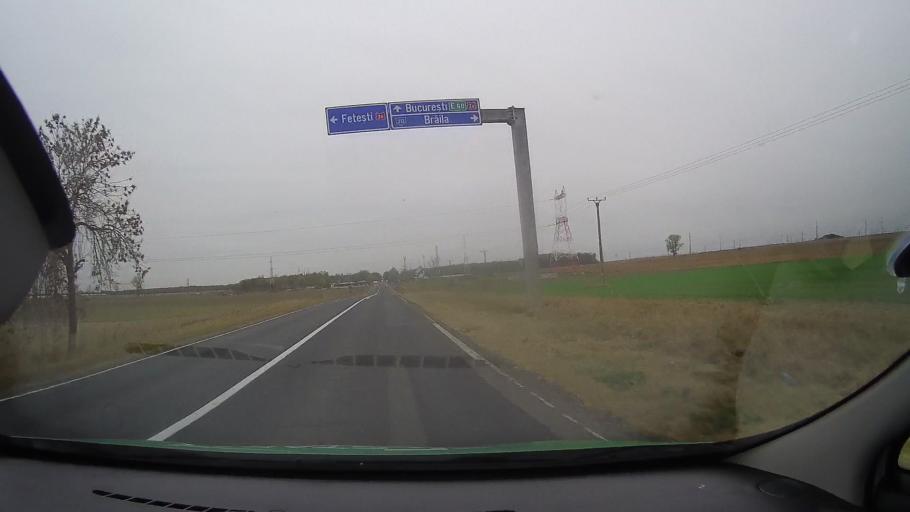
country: RO
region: Ialomita
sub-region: Comuna Gura Ialomitei
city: Gura Ialomitei
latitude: 44.6838
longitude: 27.7799
